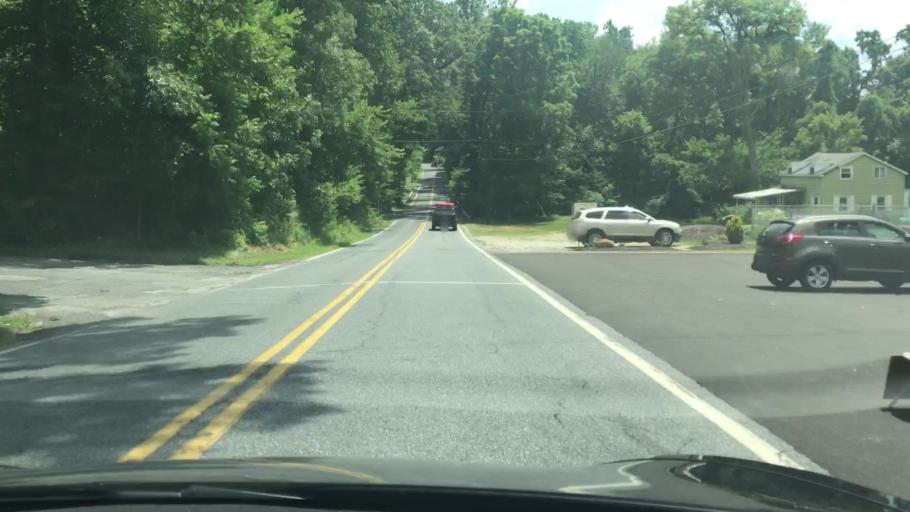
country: US
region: Pennsylvania
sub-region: York County
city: Valley Green
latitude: 40.1264
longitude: -76.7873
